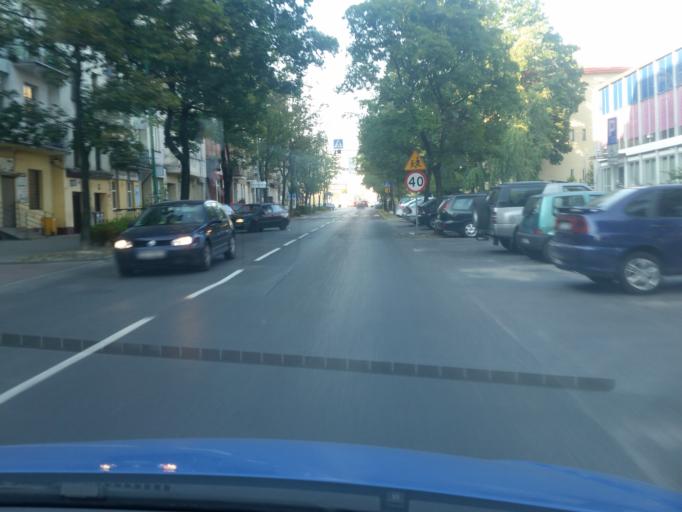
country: PL
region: Silesian Voivodeship
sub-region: Sosnowiec
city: Sosnowiec
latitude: 50.2724
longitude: 19.1290
